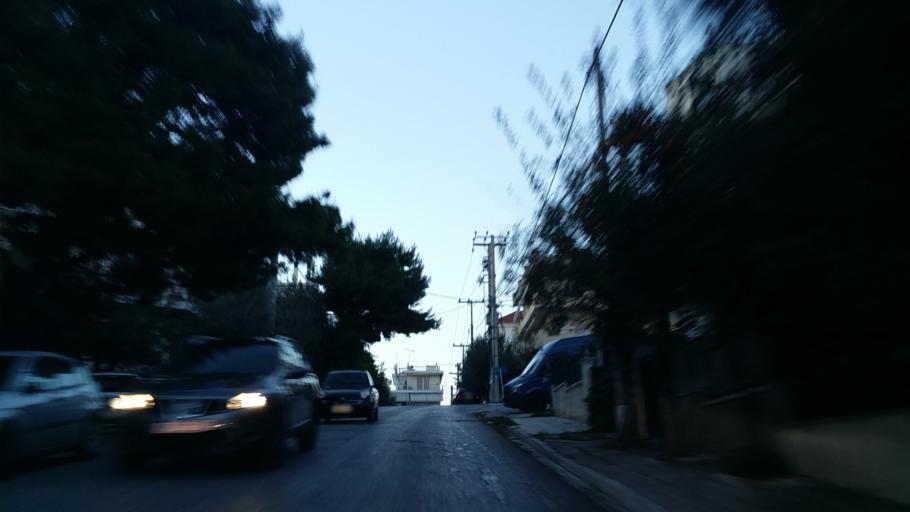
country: GR
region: Attica
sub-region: Nomarchia Athinas
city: Irakleio
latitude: 38.0546
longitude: 23.7625
